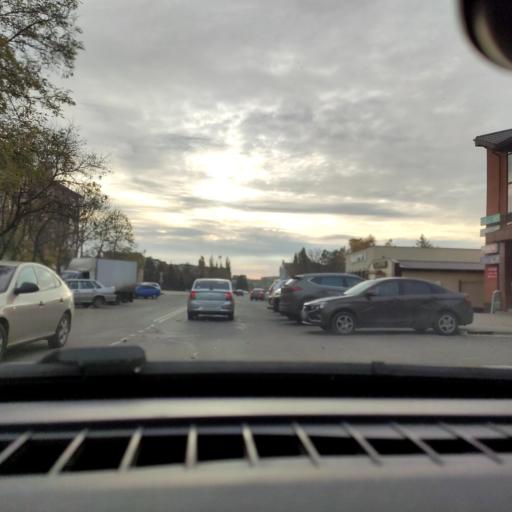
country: RU
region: Belgorod
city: Alekseyevka
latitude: 50.6307
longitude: 38.6847
